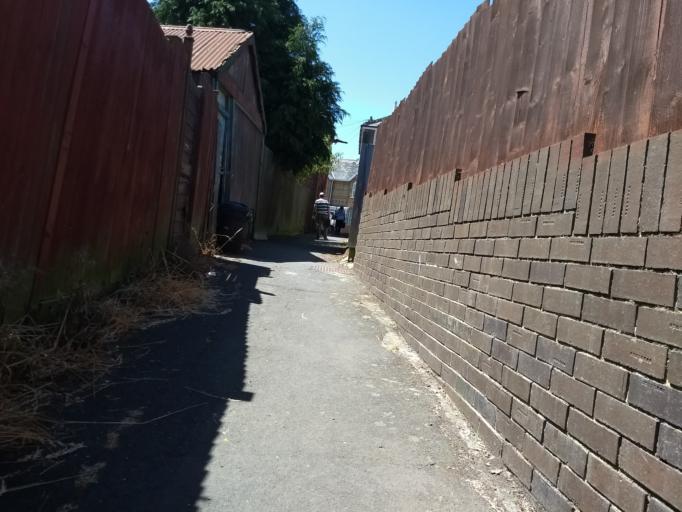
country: GB
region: England
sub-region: Isle of Wight
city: East Cowes
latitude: 50.7565
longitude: -1.2945
